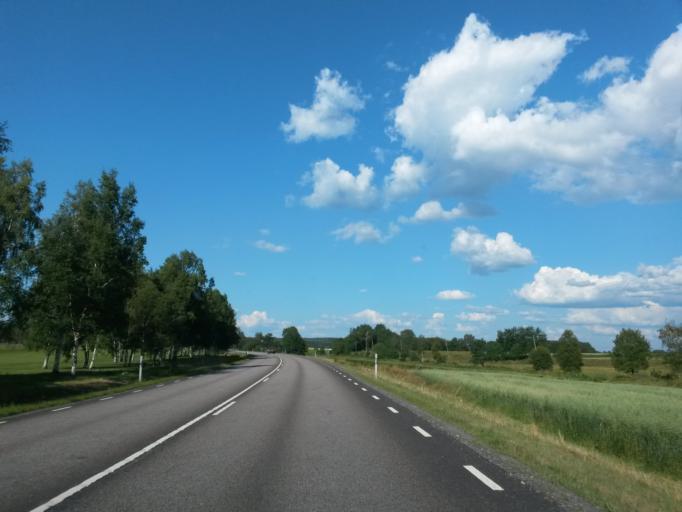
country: SE
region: Vaestra Goetaland
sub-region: Lerums Kommun
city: Olstorp
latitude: 57.8293
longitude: 12.2517
